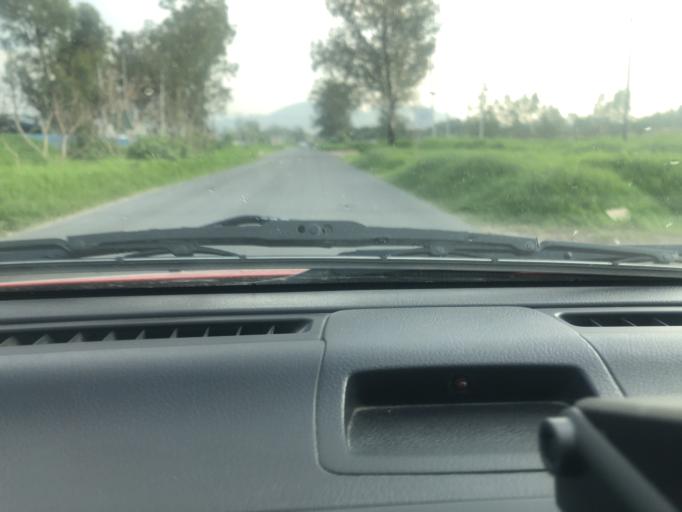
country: MX
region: Jalisco
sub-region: San Pedro Tlaquepaque
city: Paseo del Prado
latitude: 20.5756
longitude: -103.4046
